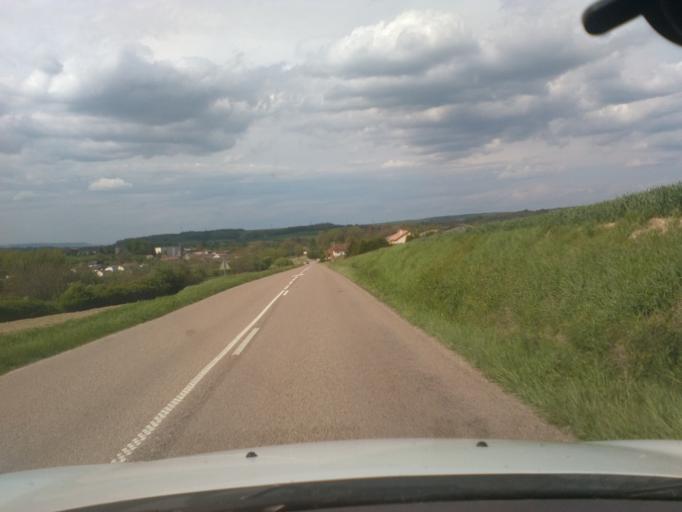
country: FR
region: Lorraine
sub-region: Departement des Vosges
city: Mirecourt
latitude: 48.2583
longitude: 6.1420
